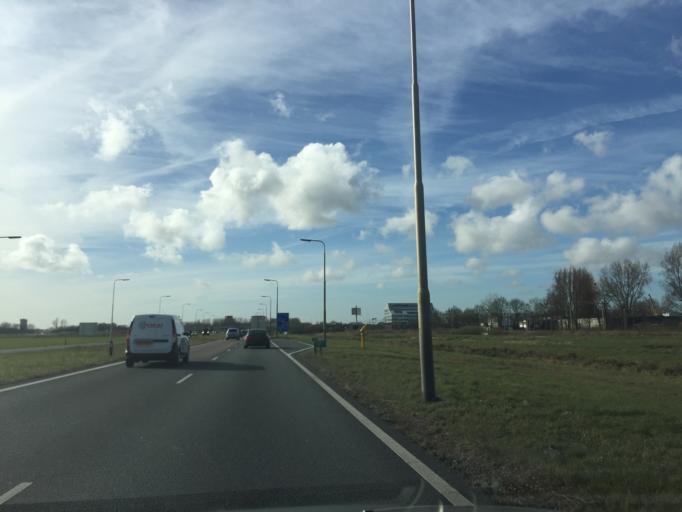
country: NL
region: South Holland
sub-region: Gemeente Leiderdorp
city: Leiderdorp
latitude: 52.1370
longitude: 4.5192
